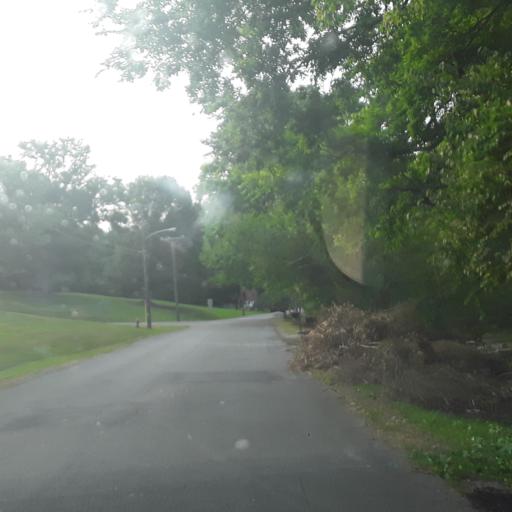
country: US
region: Tennessee
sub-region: Davidson County
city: Oak Hill
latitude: 36.0730
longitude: -86.7499
